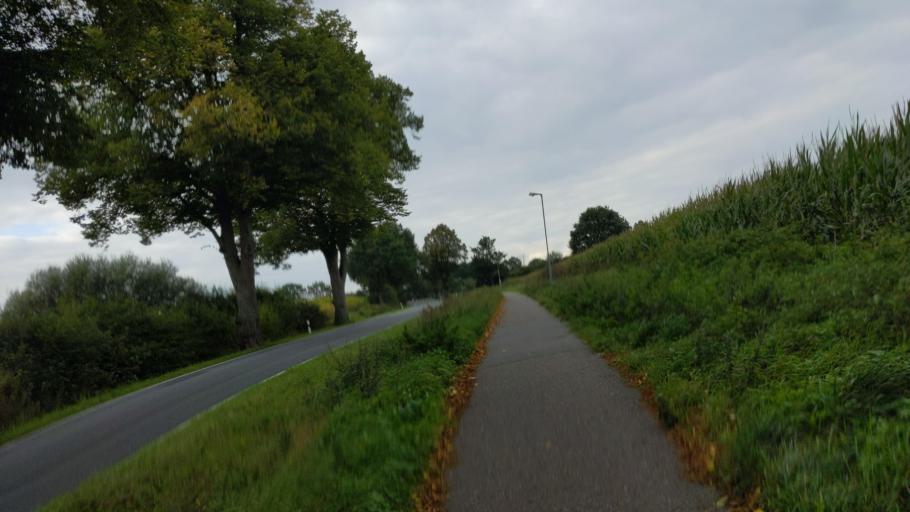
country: DE
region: Schleswig-Holstein
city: Krummesse
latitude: 53.7933
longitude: 10.6383
